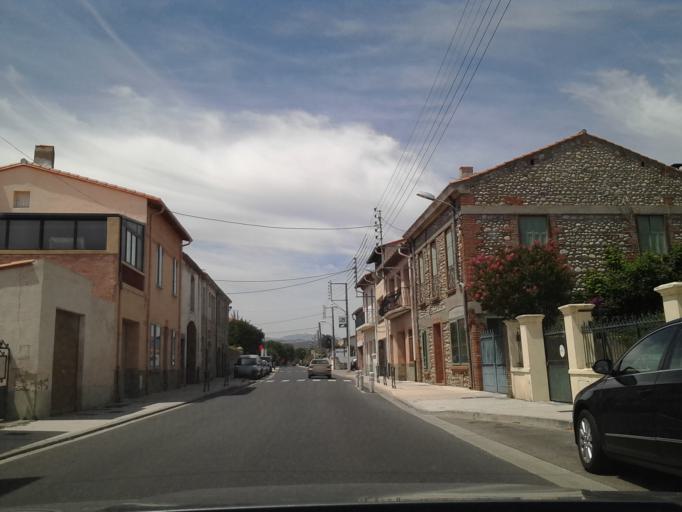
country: FR
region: Languedoc-Roussillon
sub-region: Departement des Pyrenees-Orientales
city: Millas
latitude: 42.6924
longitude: 2.6932
